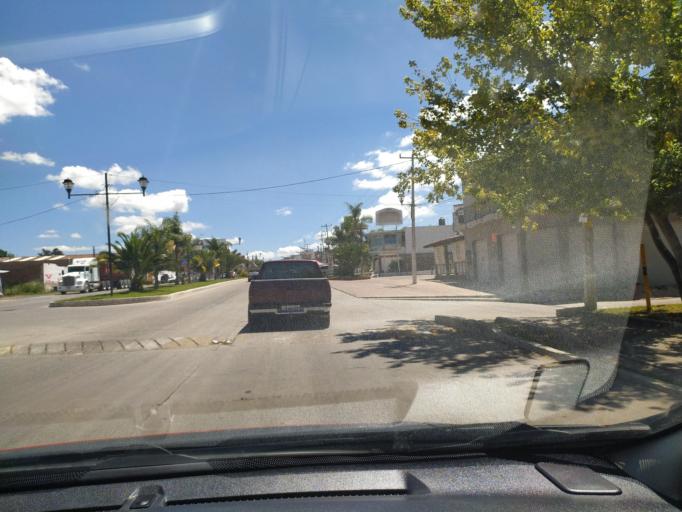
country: MX
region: Jalisco
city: San Julian
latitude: 21.0123
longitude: -102.1874
